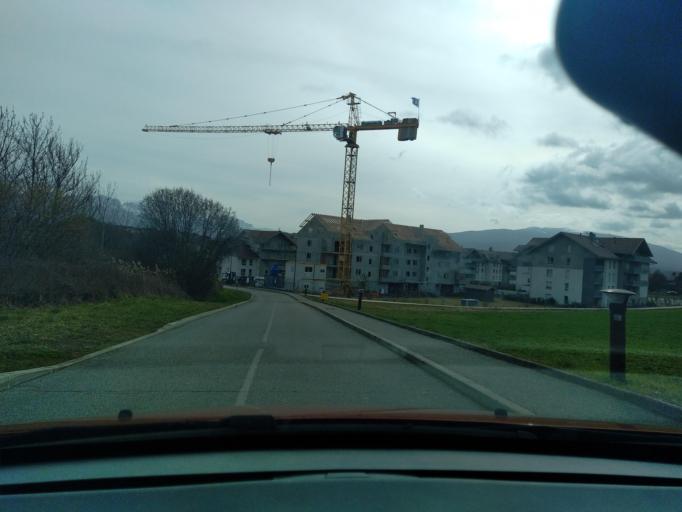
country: FR
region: Rhone-Alpes
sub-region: Departement de la Haute-Savoie
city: Poisy
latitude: 45.9270
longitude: 6.0599
